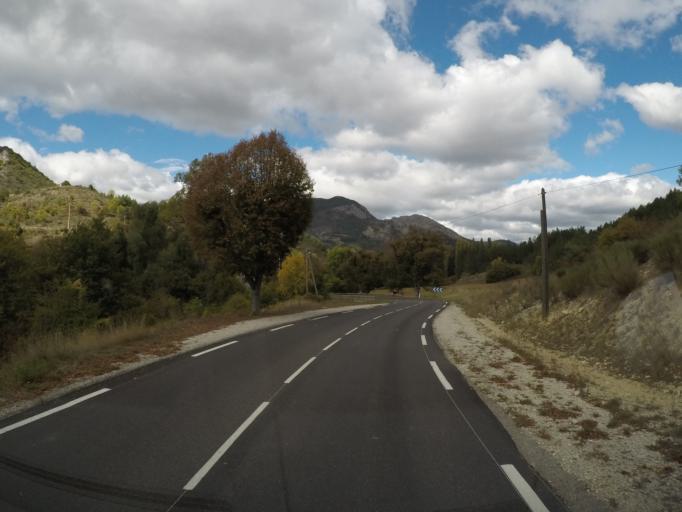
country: FR
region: Provence-Alpes-Cote d'Azur
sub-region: Departement du Vaucluse
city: Sault
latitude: 44.1871
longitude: 5.5397
